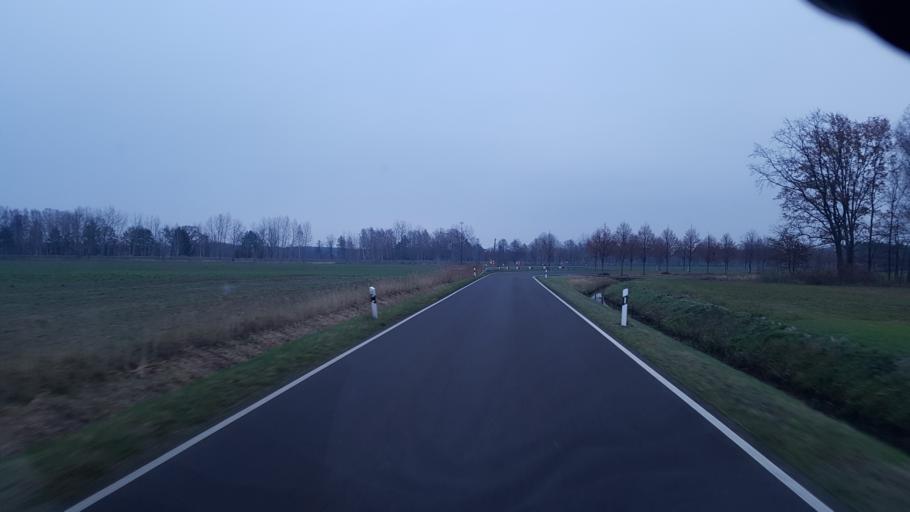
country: DE
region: Brandenburg
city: Werben
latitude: 51.8476
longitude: 14.1905
